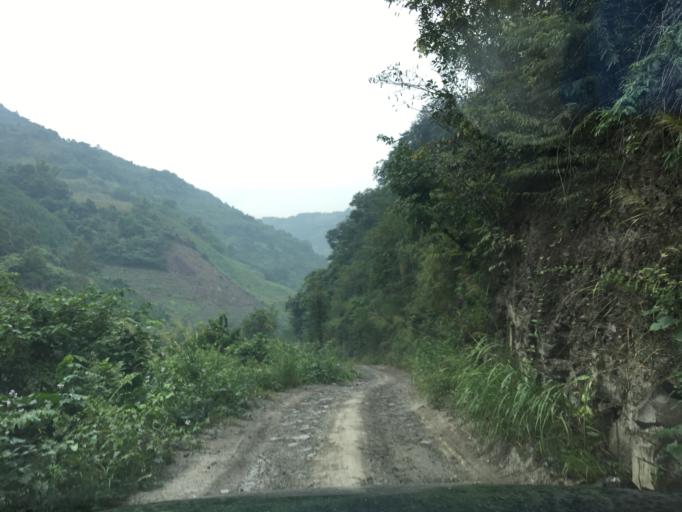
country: CN
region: Guangxi Zhuangzu Zizhiqu
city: Xinzhou
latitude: 25.0505
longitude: 105.9201
